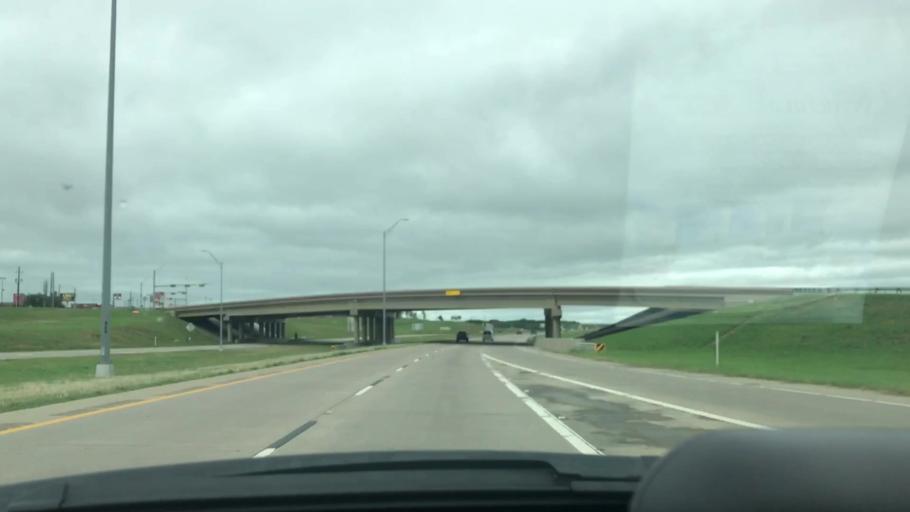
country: US
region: Texas
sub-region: Grayson County
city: Sherman
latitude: 33.6797
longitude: -96.6081
